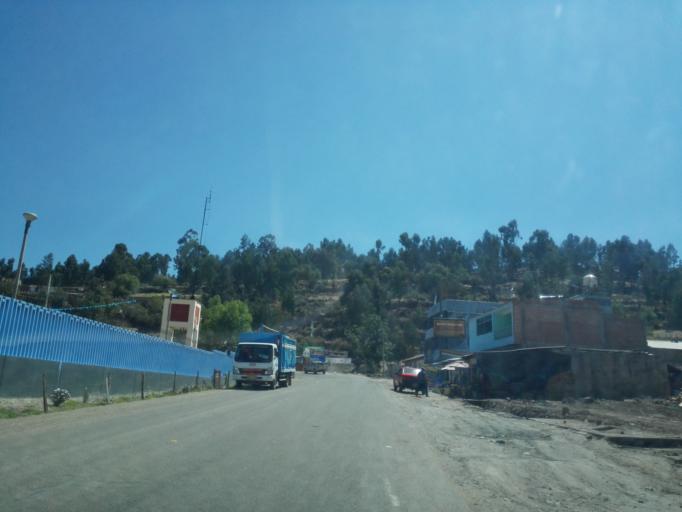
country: PE
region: Ayacucho
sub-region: Provincia de Huamanga
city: Ayacucho
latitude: -13.1646
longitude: -74.2491
